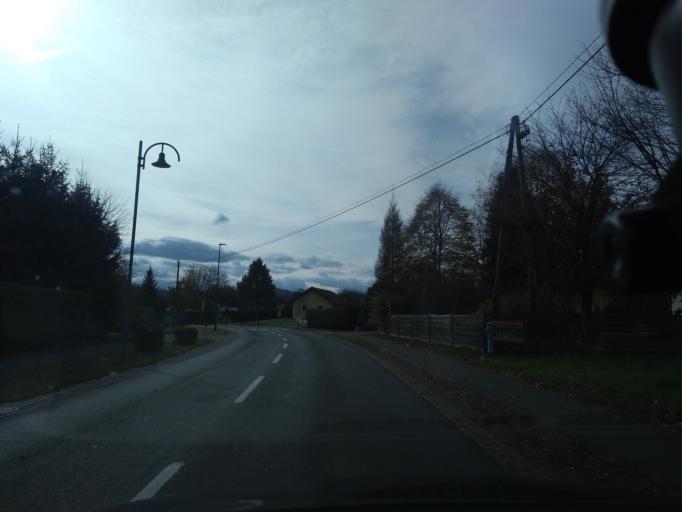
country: AT
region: Styria
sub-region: Politischer Bezirk Leibnitz
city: Heimschuh
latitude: 46.7640
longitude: 15.4941
